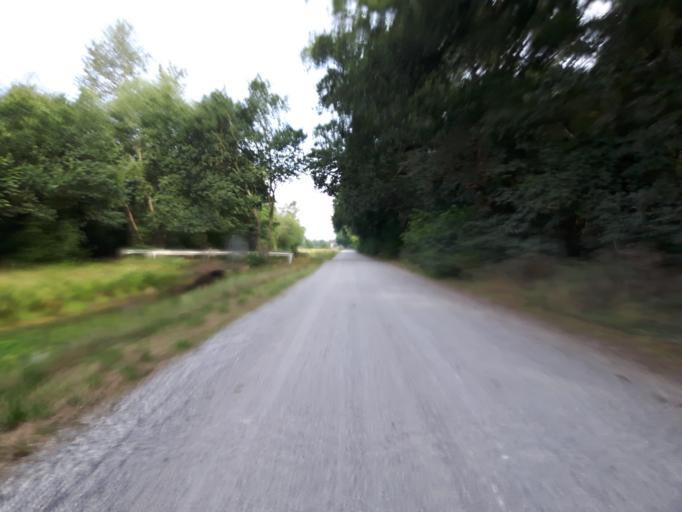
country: DE
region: Lower Saxony
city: Delmenhorst
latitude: 53.0834
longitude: 8.6298
